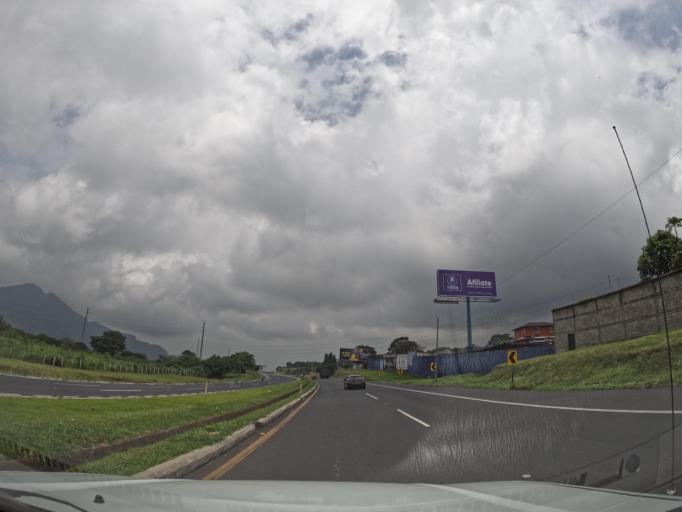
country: GT
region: Escuintla
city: Palin
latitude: 14.4072
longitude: -90.7045
